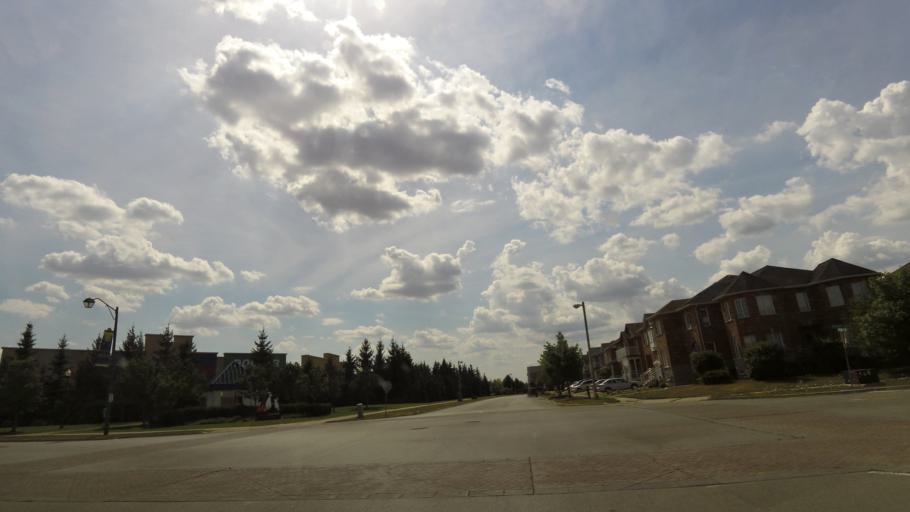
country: CA
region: Ontario
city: Vaughan
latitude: 43.7927
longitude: -79.5507
